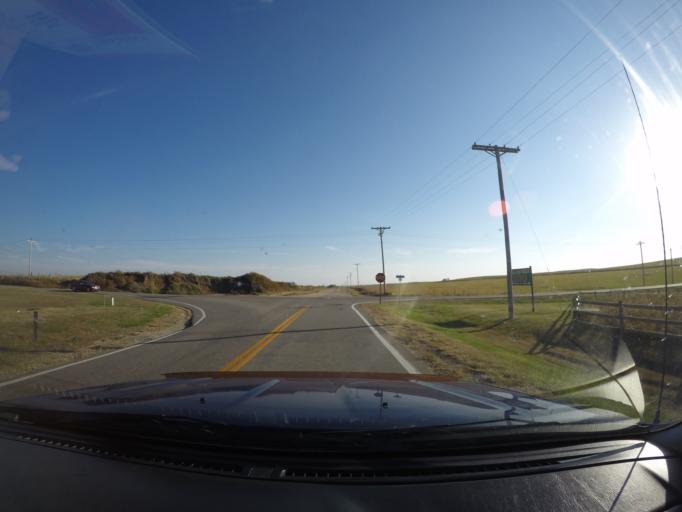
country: US
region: Kansas
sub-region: Saline County
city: Salina
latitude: 38.8422
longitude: -97.7615
